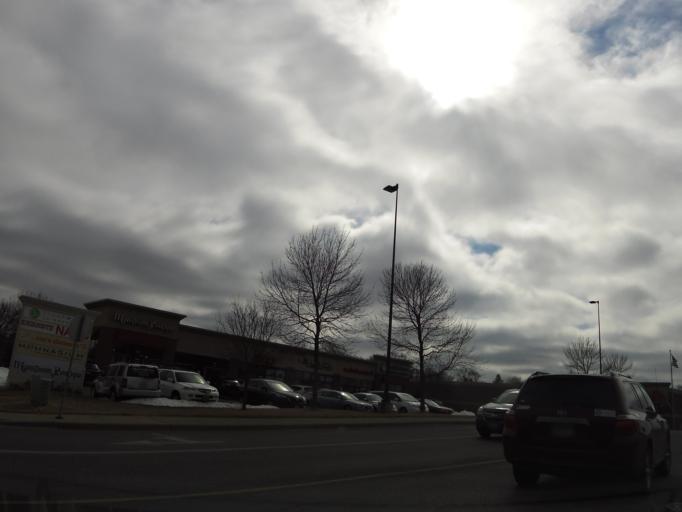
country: US
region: Minnesota
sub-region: Scott County
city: Savage
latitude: 44.7498
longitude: -93.3781
